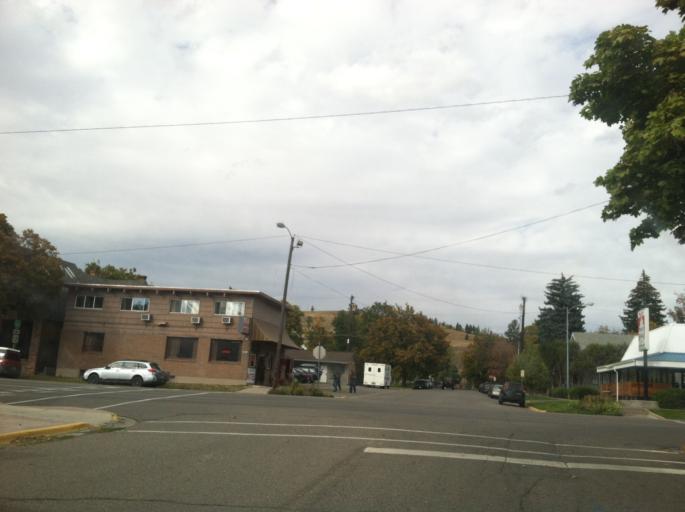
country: US
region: Montana
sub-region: Missoula County
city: Missoula
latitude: 46.8705
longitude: -113.9899
